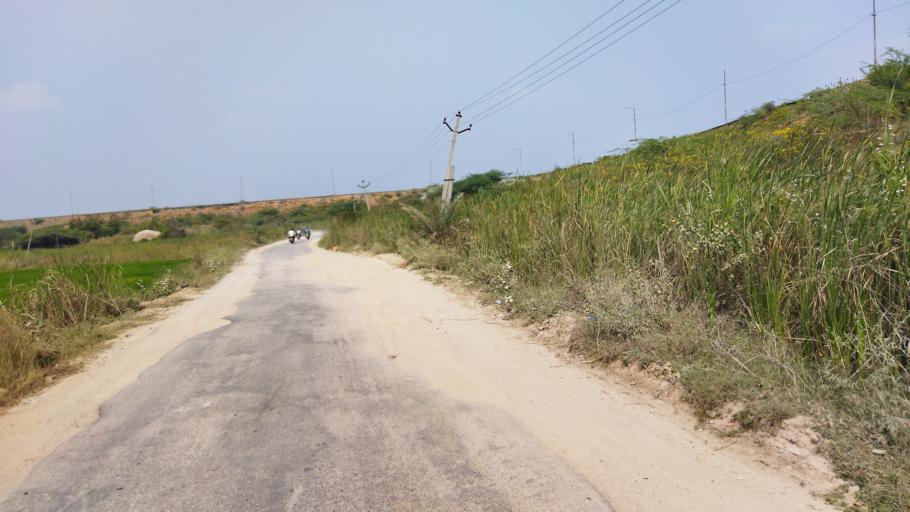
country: IN
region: Telangana
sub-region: Nalgonda
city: Nalgonda
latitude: 17.0753
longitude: 79.3144
